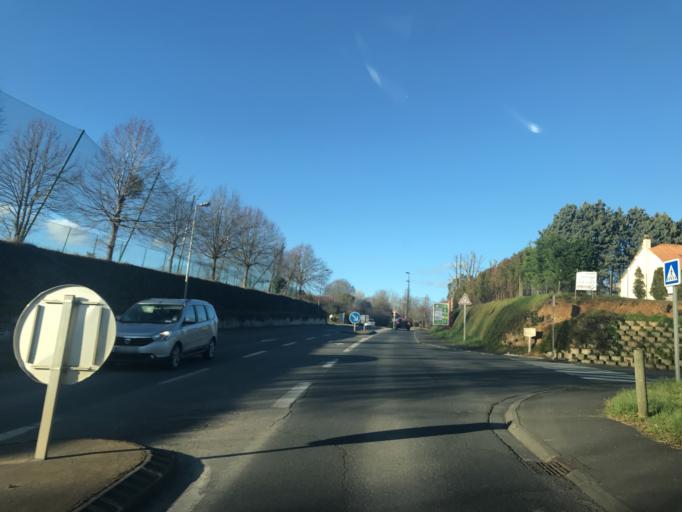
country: FR
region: Lower Normandy
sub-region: Departement du Calvados
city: Beuville
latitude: 49.2277
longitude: -0.3325
